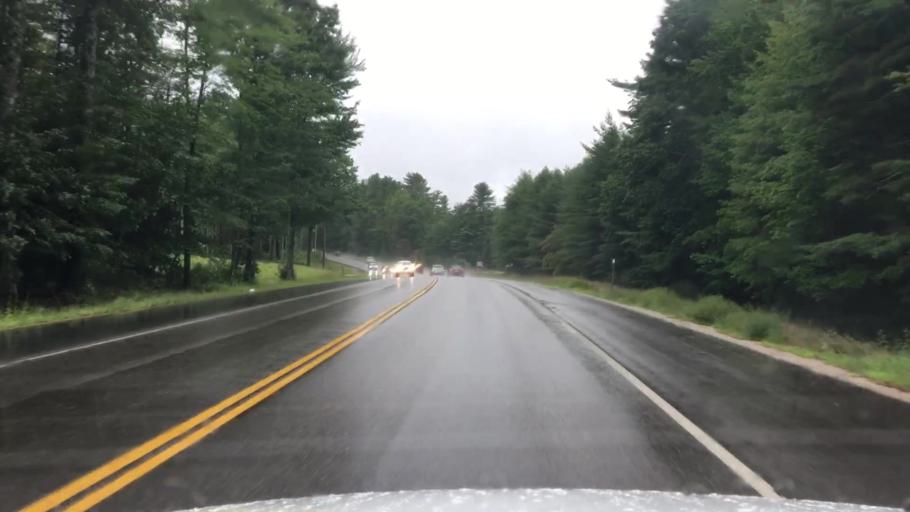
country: US
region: New Hampshire
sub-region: Carroll County
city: Conway
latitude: 43.9968
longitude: -71.0746
